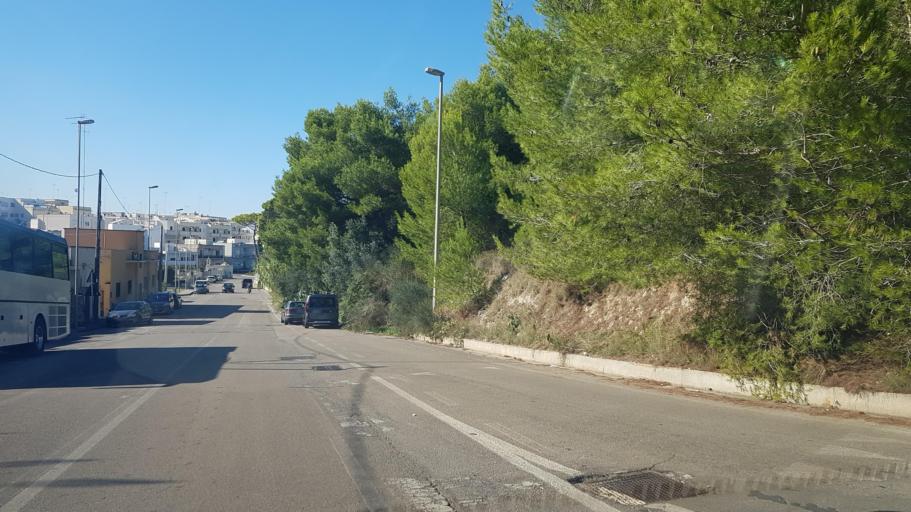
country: IT
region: Apulia
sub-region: Provincia di Lecce
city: Otranto
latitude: 40.1426
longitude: 18.4969
